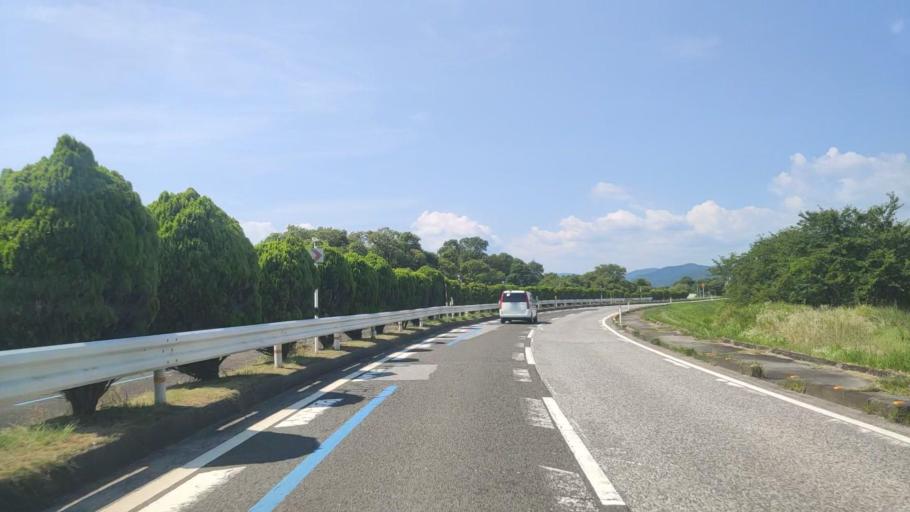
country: JP
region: Shiga Prefecture
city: Nagahama
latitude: 35.4260
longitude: 136.1964
